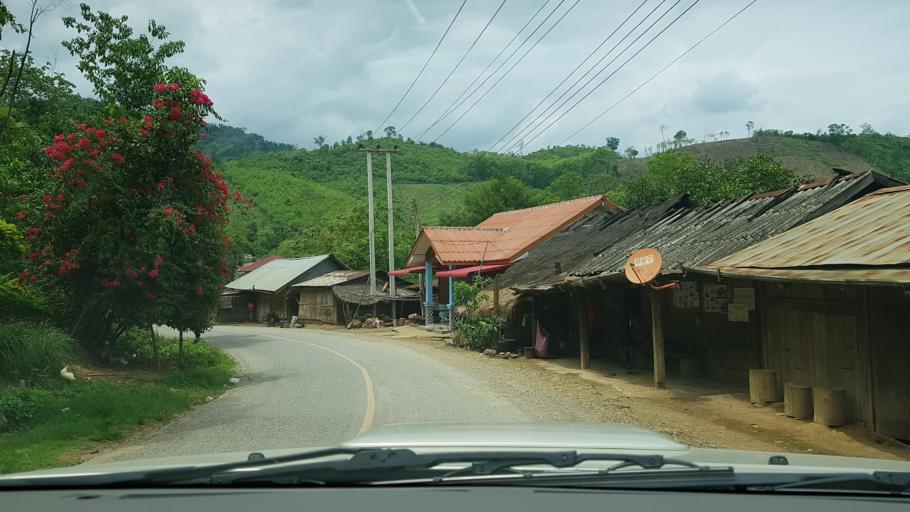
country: TH
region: Nan
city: Chaloem Phra Kiat
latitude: 19.9632
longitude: 101.2636
